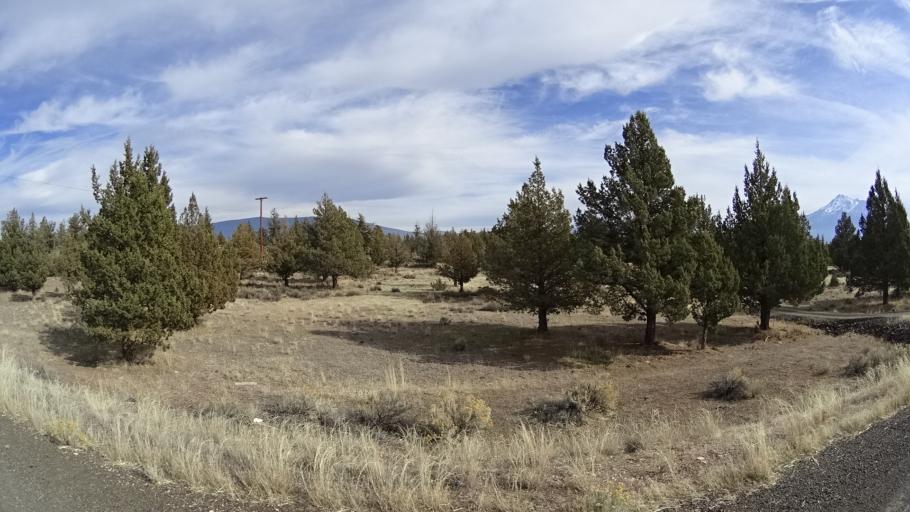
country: US
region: California
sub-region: Siskiyou County
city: Weed
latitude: 41.5878
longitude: -122.4000
